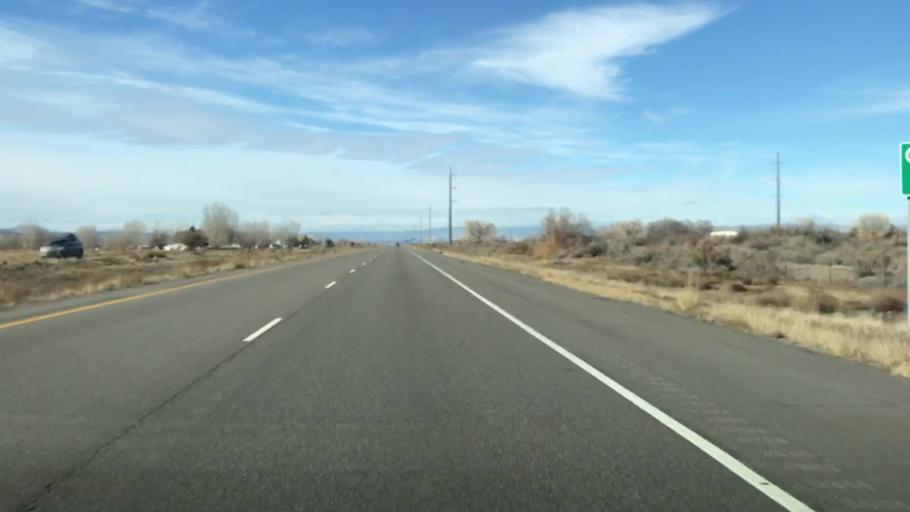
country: US
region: Colorado
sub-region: Mesa County
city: Fruita
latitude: 39.1381
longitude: -108.7016
